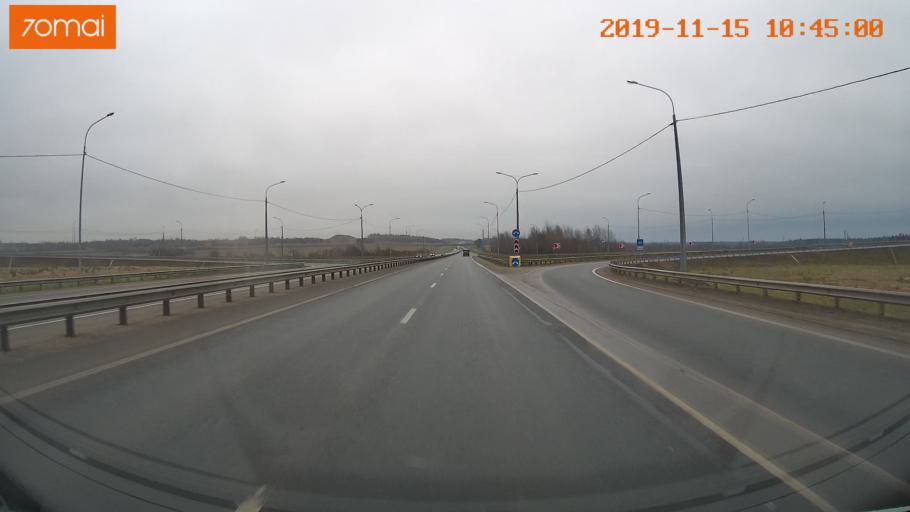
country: RU
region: Vologda
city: Sheksna
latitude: 59.2113
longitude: 38.5744
